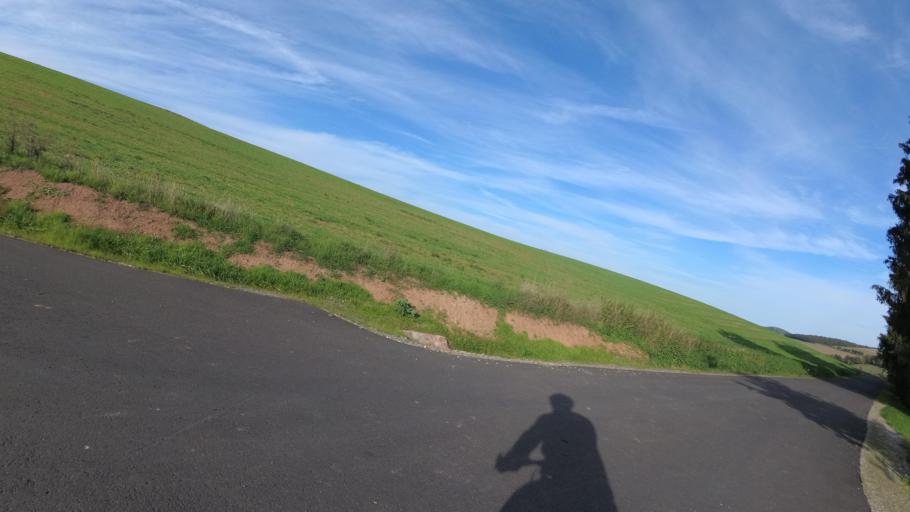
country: DE
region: Rheinland-Pfalz
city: Wahnwegen
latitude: 49.4564
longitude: 7.3814
